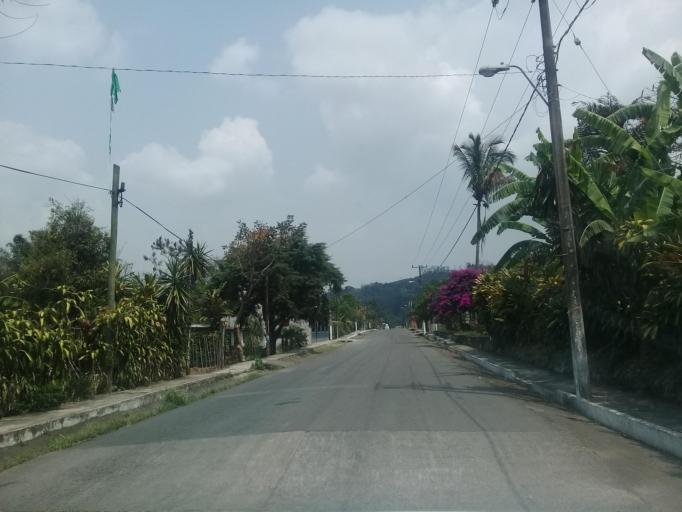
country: MX
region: Veracruz
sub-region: Cordoba
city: San Jose de Tapia
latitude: 18.8211
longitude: -96.9806
